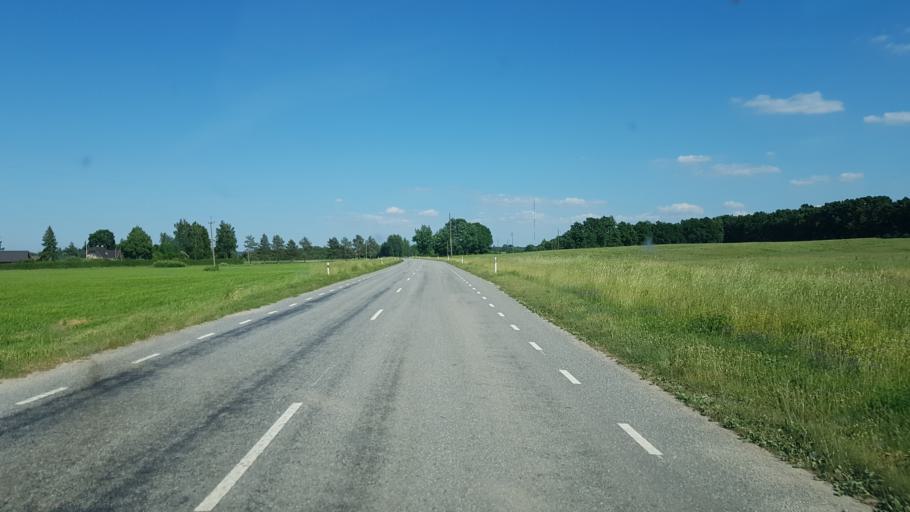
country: EE
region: Vorumaa
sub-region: Voru linn
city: Voru
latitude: 57.8561
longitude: 27.1622
